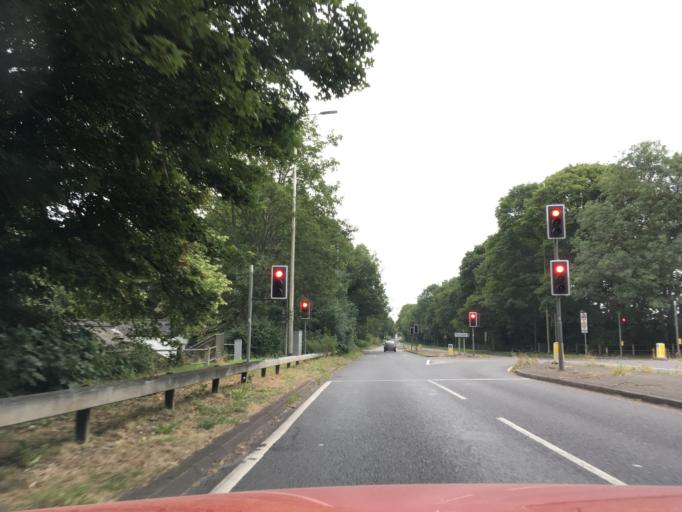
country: GB
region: England
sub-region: Hertfordshire
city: Markyate
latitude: 51.8398
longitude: -0.4639
